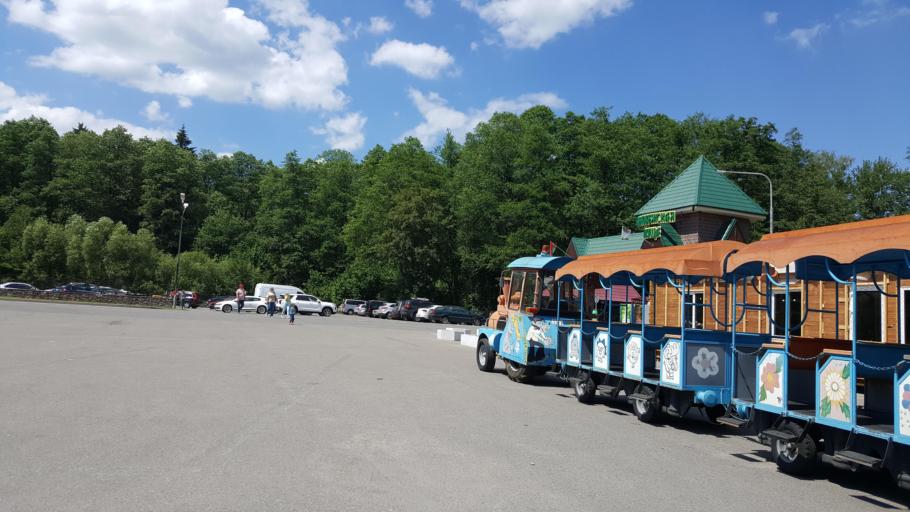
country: BY
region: Brest
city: Kamyanyuki
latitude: 52.5691
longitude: 23.8034
